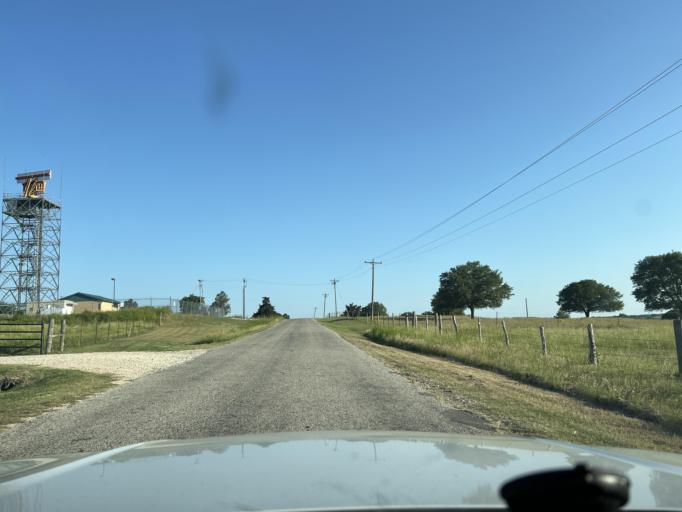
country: US
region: Texas
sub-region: Washington County
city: Brenham
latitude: 30.2285
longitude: -96.3798
